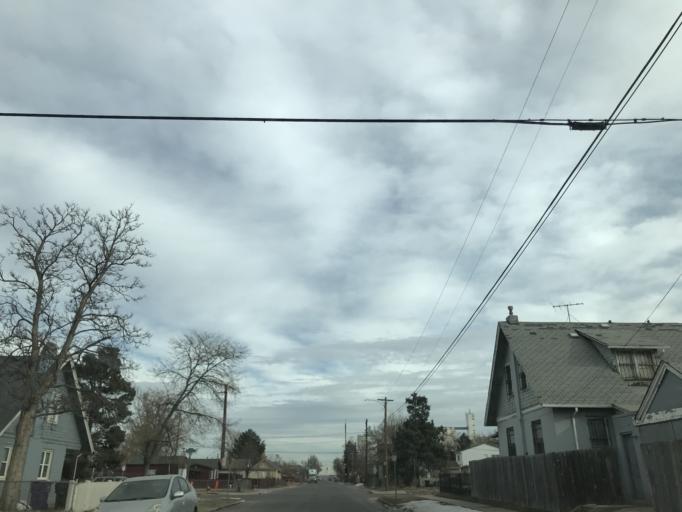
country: US
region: Colorado
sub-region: Adams County
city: Commerce City
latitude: 39.7789
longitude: -104.9537
